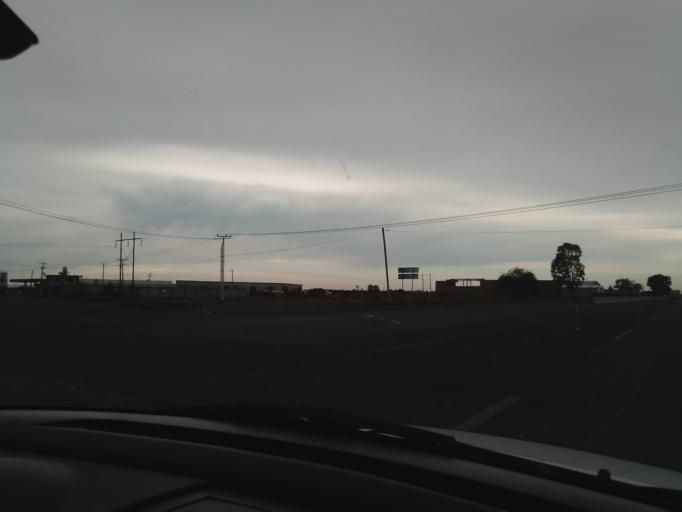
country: MX
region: Guanajuato
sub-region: Dolores Hidalgo Cuna de la Independencia Nacional
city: Ejido Jesus Maria
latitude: 21.1927
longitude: -100.8671
